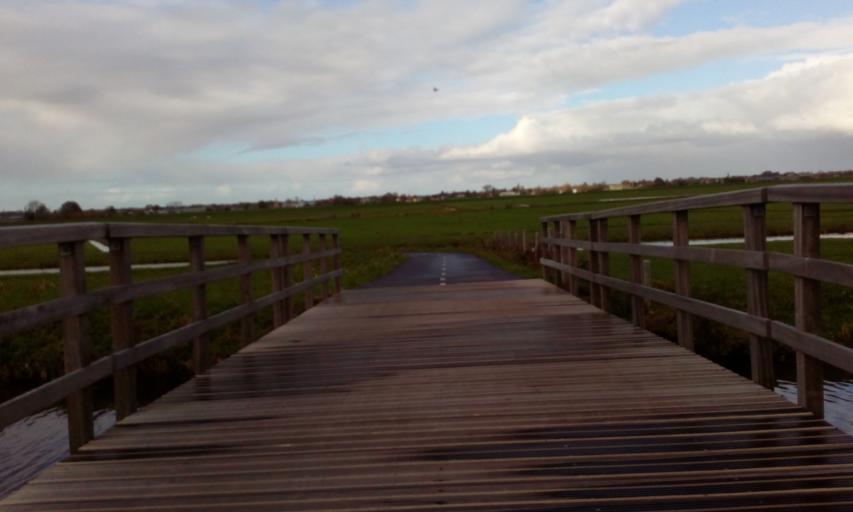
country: NL
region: South Holland
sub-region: Gemeente Pijnacker-Nootdorp
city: Pijnacker
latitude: 51.9781
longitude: 4.4357
